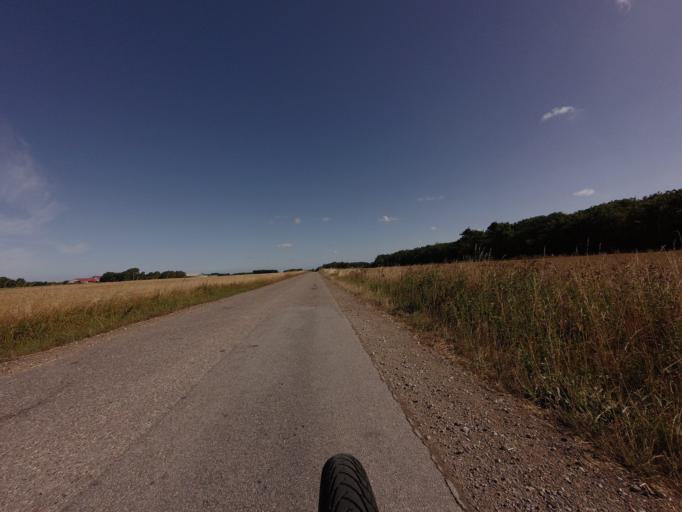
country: DK
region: North Denmark
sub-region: Hjorring Kommune
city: Vra
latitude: 57.3963
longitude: 9.9536
